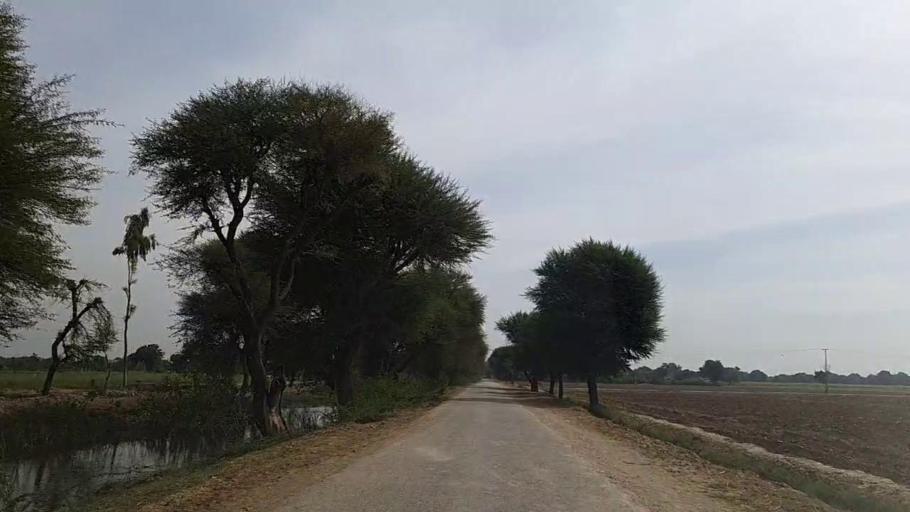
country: PK
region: Sindh
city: Samaro
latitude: 25.2873
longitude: 69.4135
